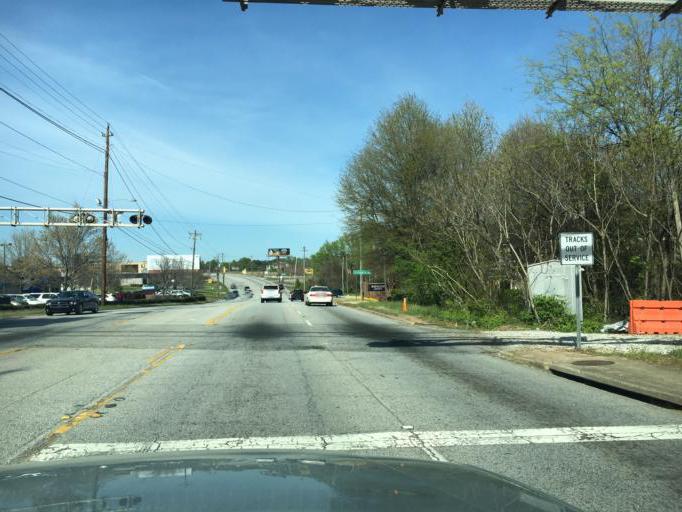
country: US
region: South Carolina
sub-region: Greenville County
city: Greenville
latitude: 34.8349
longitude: -82.3468
